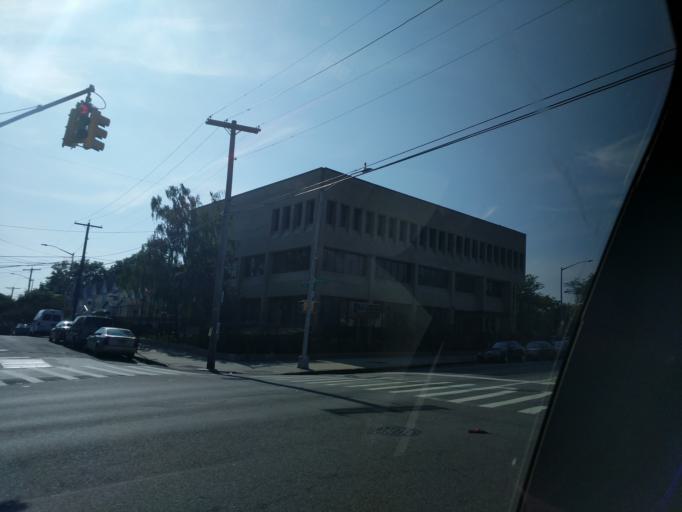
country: US
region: New York
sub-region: Queens County
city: Jamaica
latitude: 40.6883
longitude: -73.7765
